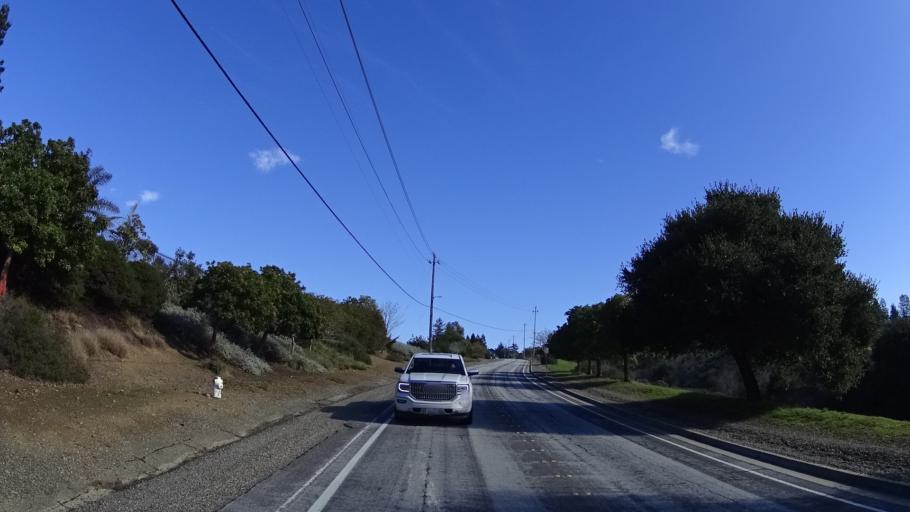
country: US
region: California
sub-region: Alameda County
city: Fairview
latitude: 37.6753
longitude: -122.0399
